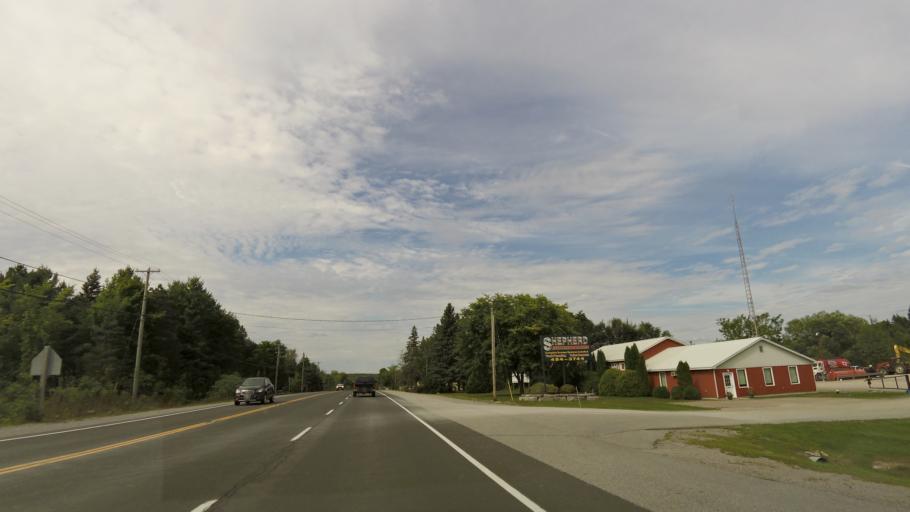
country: CA
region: Ontario
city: Omemee
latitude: 44.6695
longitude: -78.8034
